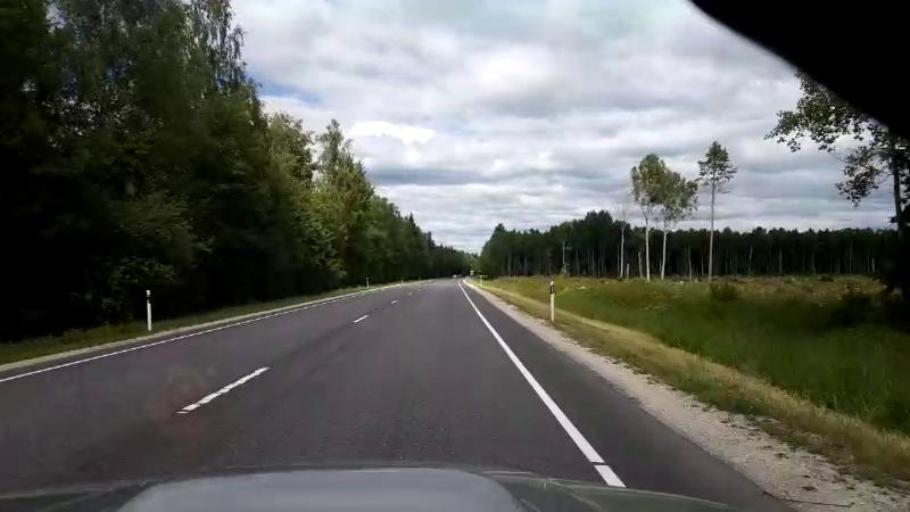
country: EE
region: Raplamaa
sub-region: Maerjamaa vald
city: Marjamaa
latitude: 58.8239
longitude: 24.4143
